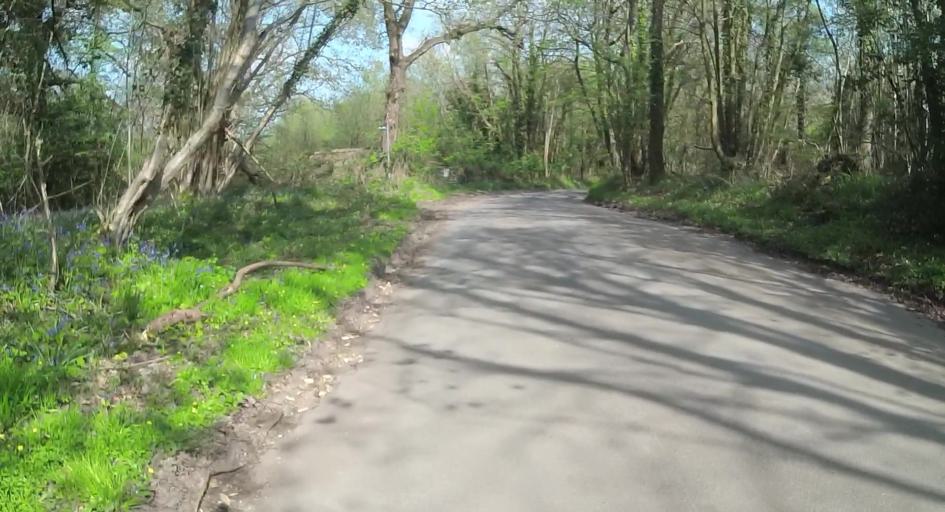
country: GB
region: England
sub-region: Hampshire
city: Tadley
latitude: 51.3892
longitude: -1.1261
